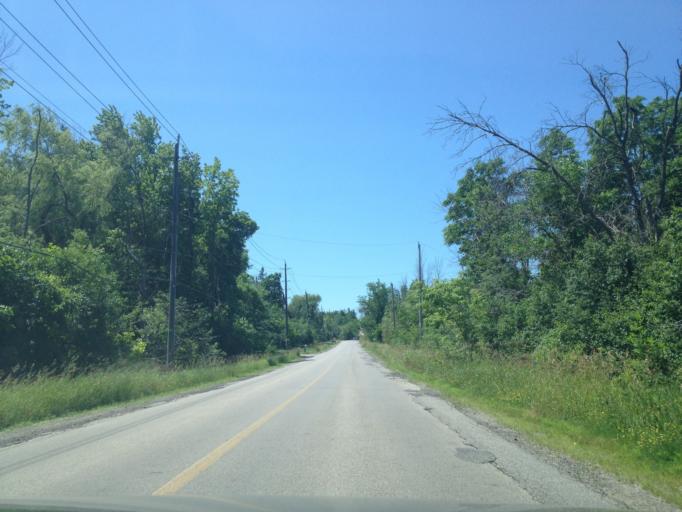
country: CA
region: Ontario
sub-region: Halton
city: Milton
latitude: 43.6639
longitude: -79.9500
